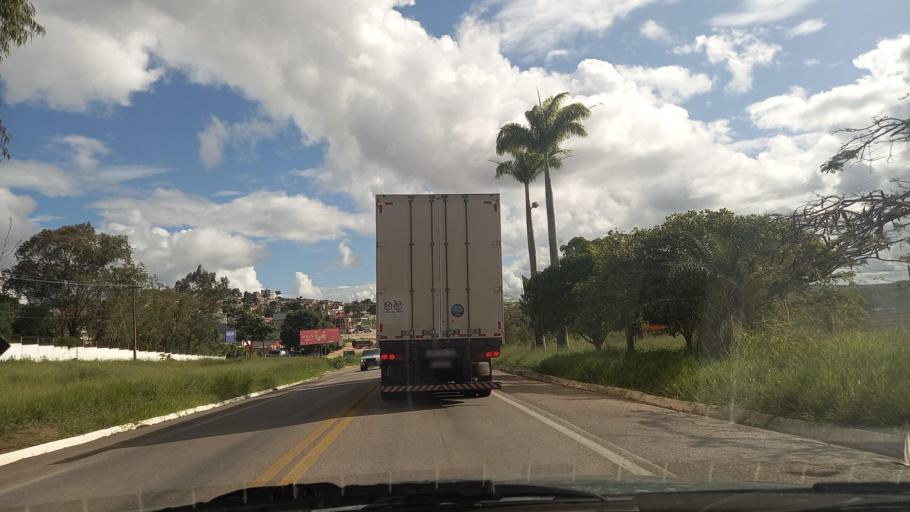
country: BR
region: Pernambuco
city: Garanhuns
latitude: -8.8703
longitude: -36.4642
